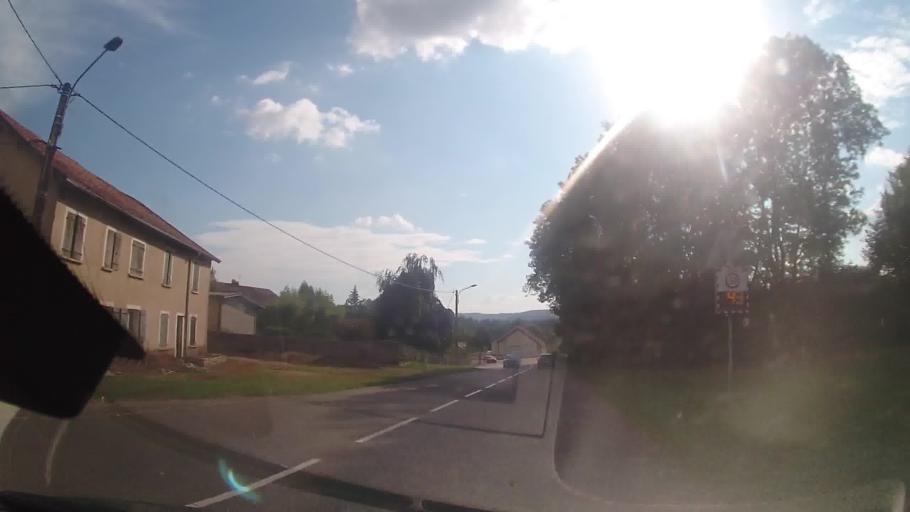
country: FR
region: Franche-Comte
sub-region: Departement du Jura
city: Clairvaux-les-Lacs
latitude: 46.5874
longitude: 5.7054
